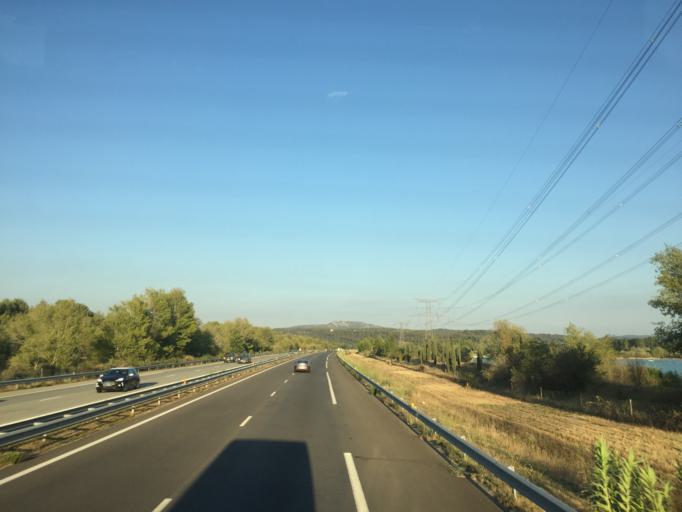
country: FR
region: Provence-Alpes-Cote d'Azur
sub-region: Departement des Bouches-du-Rhone
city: Peyrolles-en-Provence
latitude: 43.6583
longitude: 5.5844
